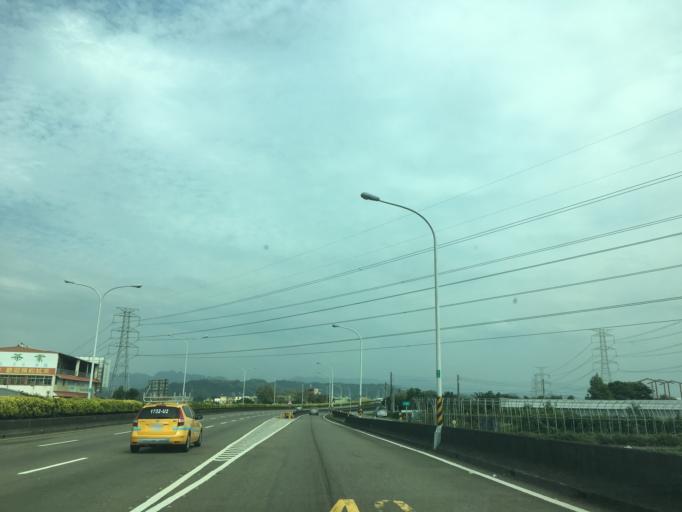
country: TW
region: Taiwan
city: Zhongxing New Village
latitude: 24.0459
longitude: 120.6665
